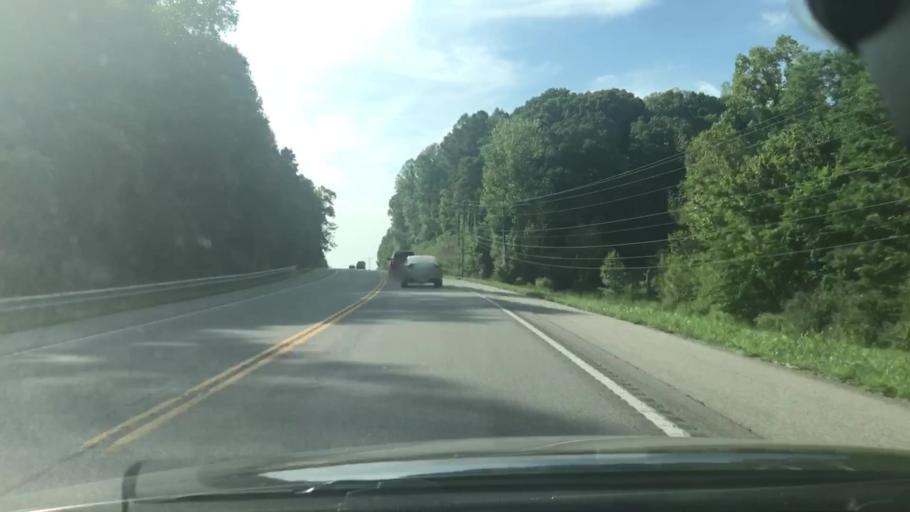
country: US
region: Tennessee
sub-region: Williamson County
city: Franklin
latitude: 35.9678
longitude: -86.9705
